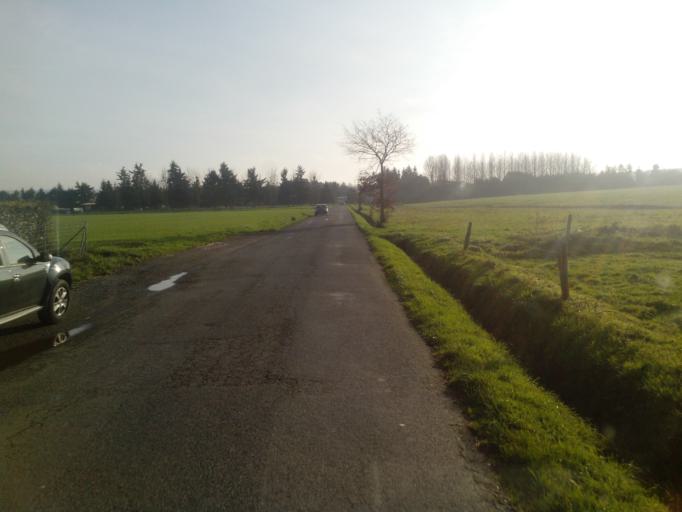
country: FR
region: Brittany
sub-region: Departement du Morbihan
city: Mauron
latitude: 48.0820
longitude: -2.2932
